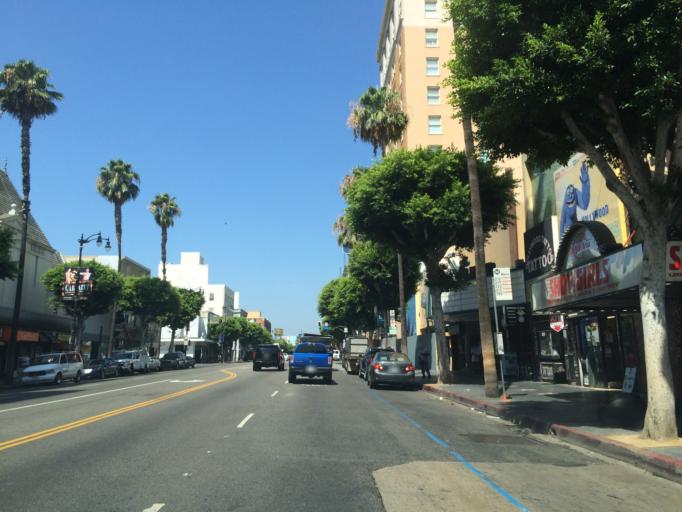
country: US
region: California
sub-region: Los Angeles County
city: Hollywood
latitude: 34.1017
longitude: -118.3271
